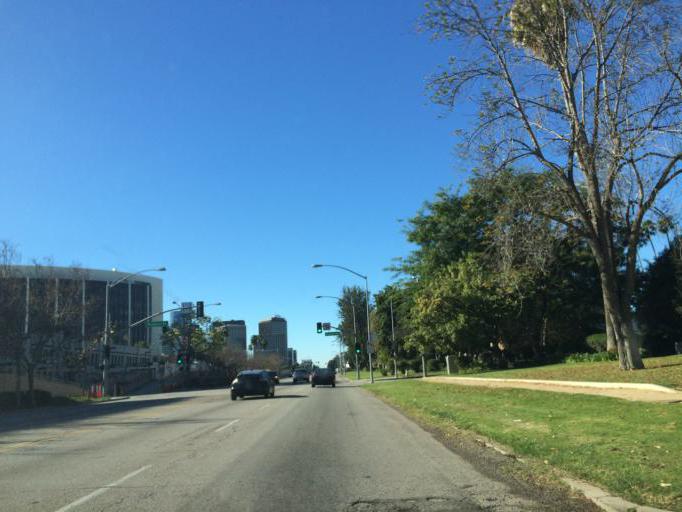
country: US
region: California
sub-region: Los Angeles County
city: Beverly Hills
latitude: 34.0694
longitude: -118.4071
